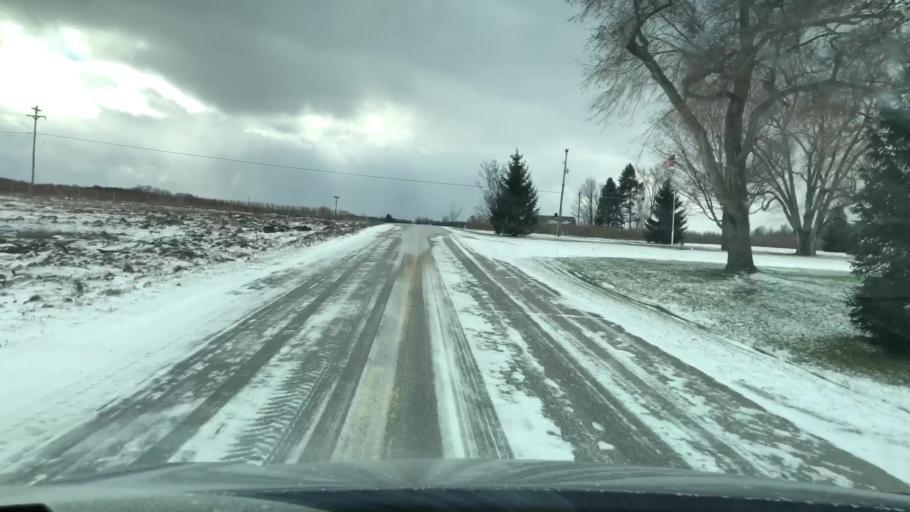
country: US
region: Michigan
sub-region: Antrim County
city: Elk Rapids
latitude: 44.9219
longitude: -85.5156
